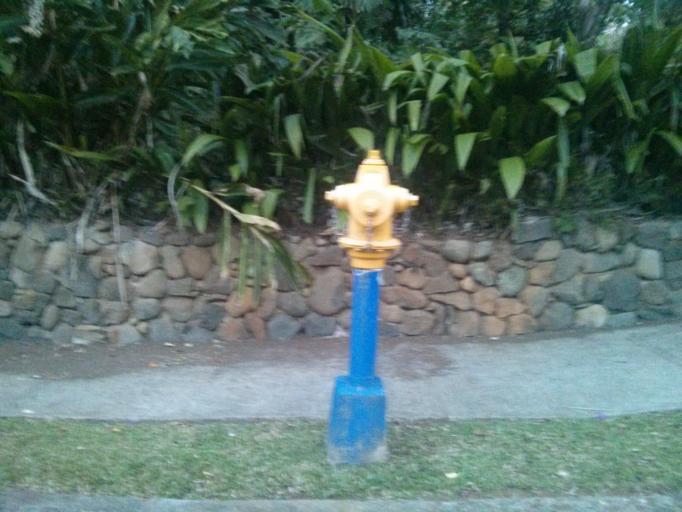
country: CR
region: Heredia
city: Angeles
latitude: 10.0194
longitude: -84.0471
